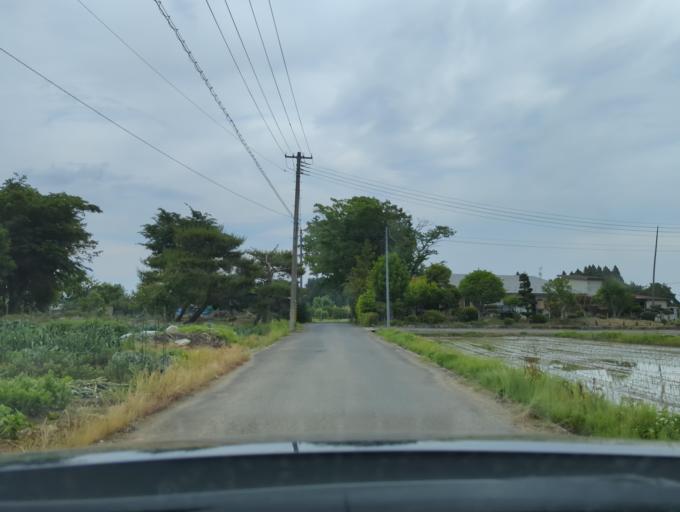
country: JP
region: Fukushima
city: Koriyama
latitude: 37.3768
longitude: 140.3032
